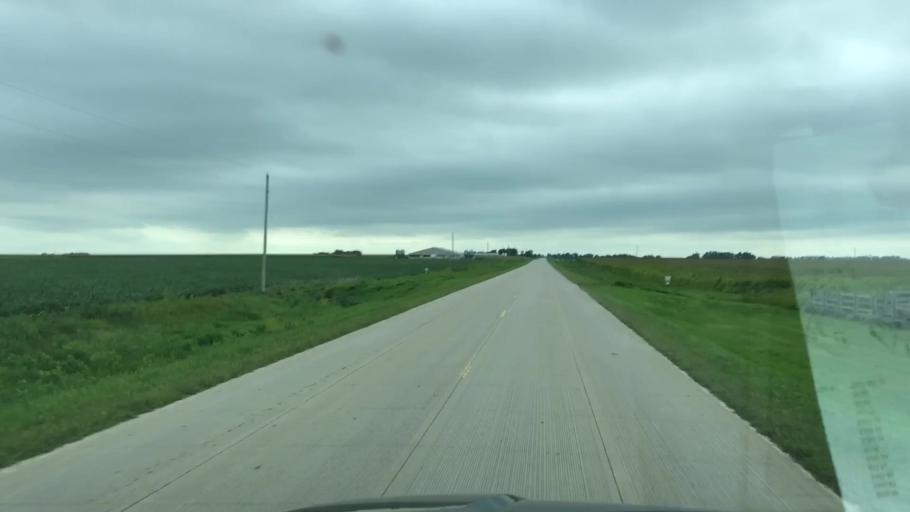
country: US
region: Iowa
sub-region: O'Brien County
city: Sheldon
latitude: 43.1319
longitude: -95.9792
